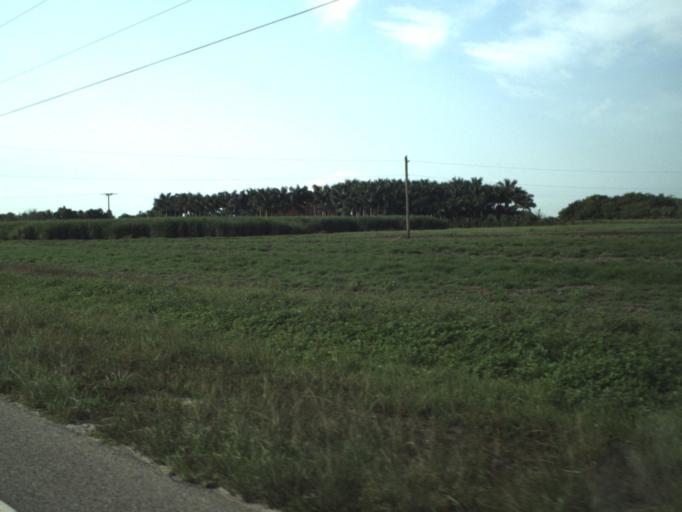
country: US
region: Florida
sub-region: Hendry County
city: Clewiston
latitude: 26.7069
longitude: -80.8313
